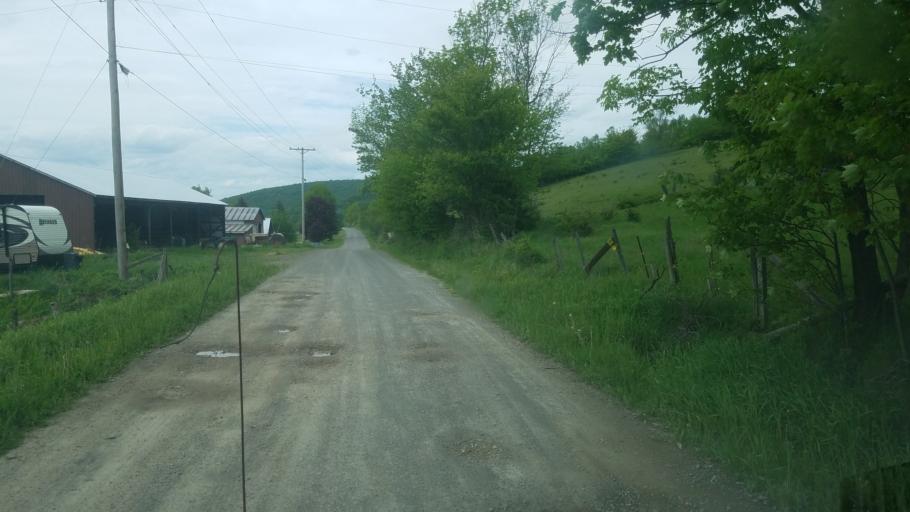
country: US
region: Pennsylvania
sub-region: Tioga County
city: Westfield
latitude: 41.8723
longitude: -77.5962
